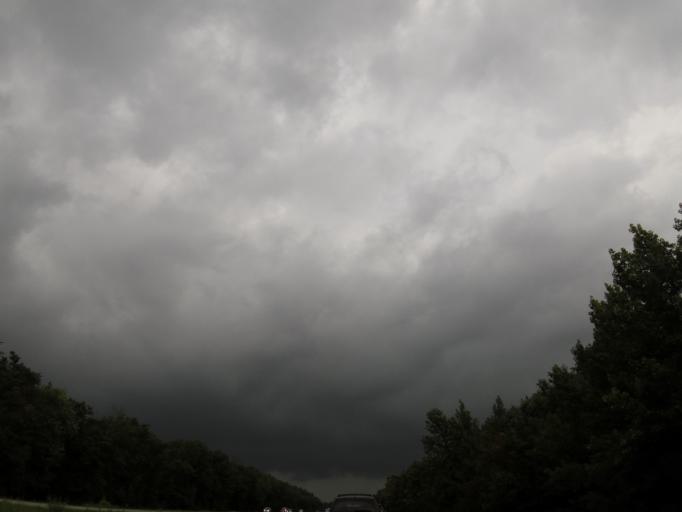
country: US
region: Illinois
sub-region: Jefferson County
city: Mount Vernon
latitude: 38.2392
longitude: -88.9060
